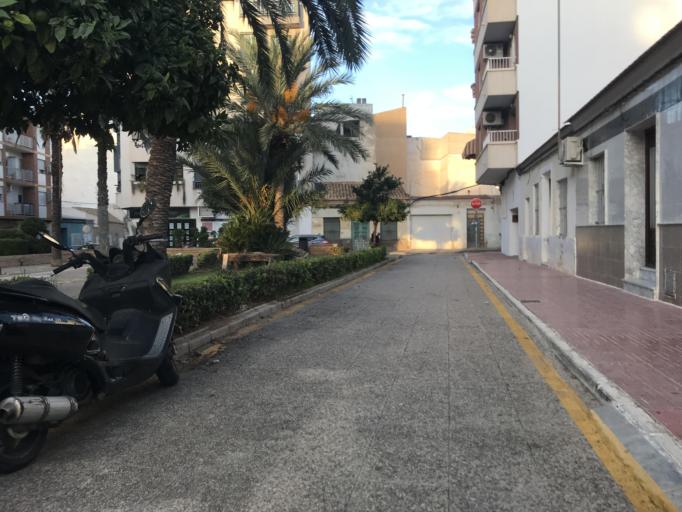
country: ES
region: Valencia
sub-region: Provincia de Alicante
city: Torrevieja
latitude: 37.9800
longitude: -0.6845
